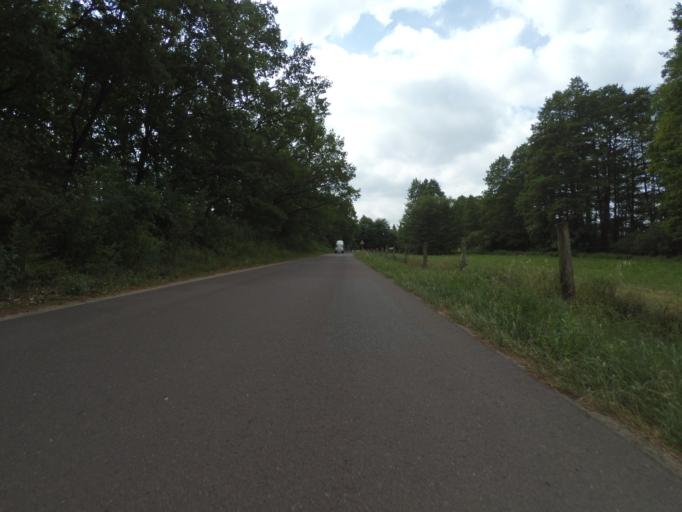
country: DE
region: Mecklenburg-Vorpommern
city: Grabowhofe
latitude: 53.5341
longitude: 12.5582
